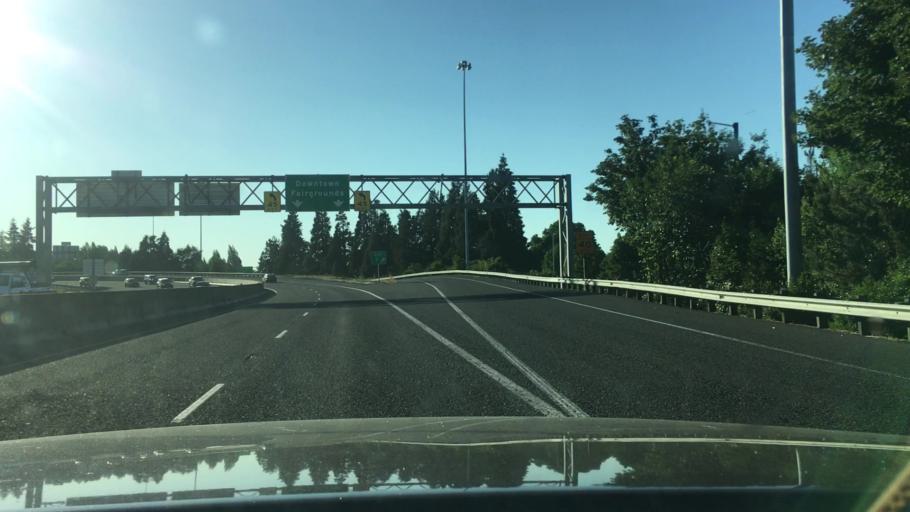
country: US
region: Oregon
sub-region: Lane County
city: Eugene
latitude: 44.0641
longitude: -123.0963
